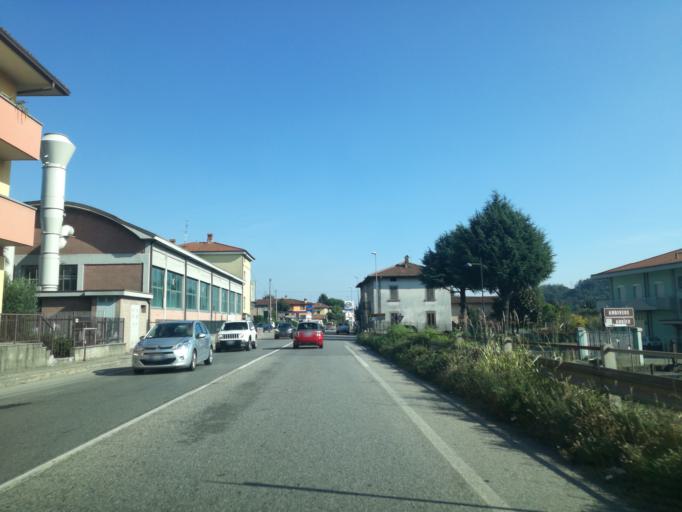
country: IT
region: Lombardy
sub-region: Provincia di Bergamo
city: Gromlongo
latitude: 45.7298
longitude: 9.5274
